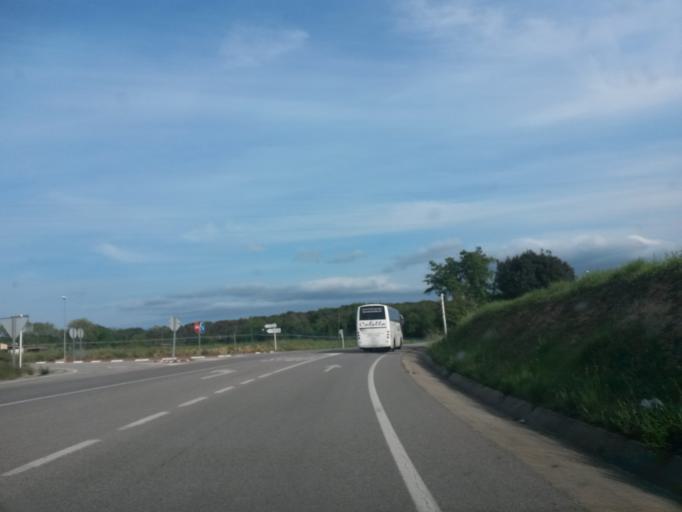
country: ES
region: Catalonia
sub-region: Provincia de Girona
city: Vidreres
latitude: 41.8029
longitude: 2.7700
